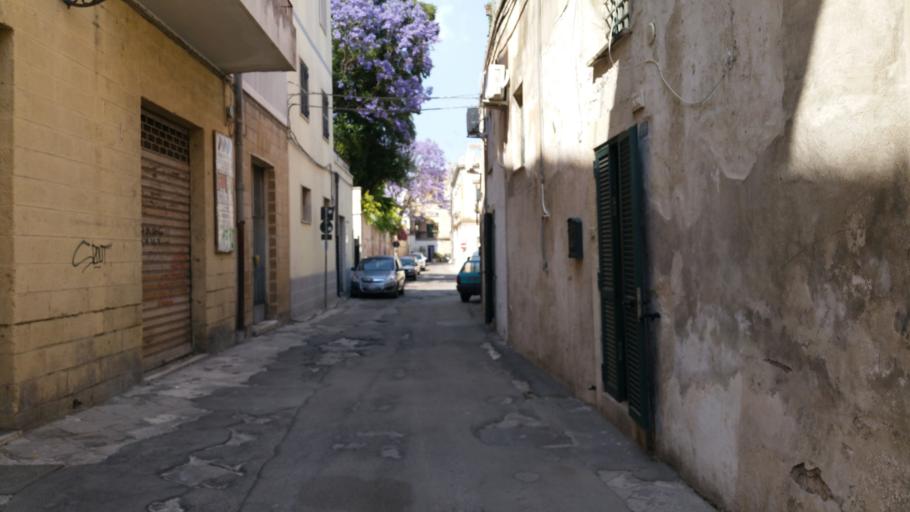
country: IT
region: Apulia
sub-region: Provincia di Lecce
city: Lecce
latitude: 40.3539
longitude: 18.1671
